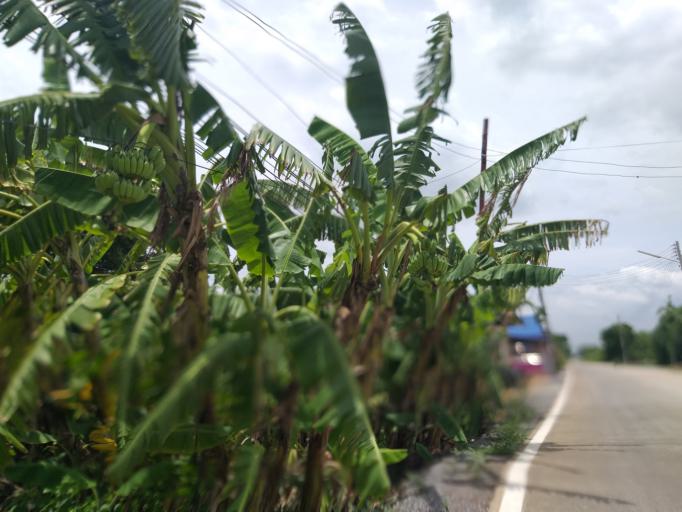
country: TH
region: Pathum Thani
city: Ban Lam Luk Ka
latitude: 13.9851
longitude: 100.8533
